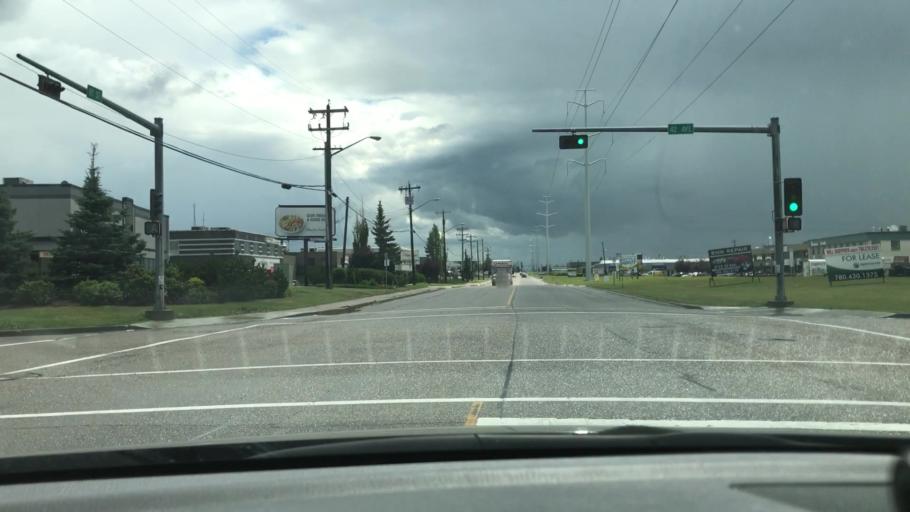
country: CA
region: Alberta
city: Edmonton
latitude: 53.4790
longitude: -113.4792
